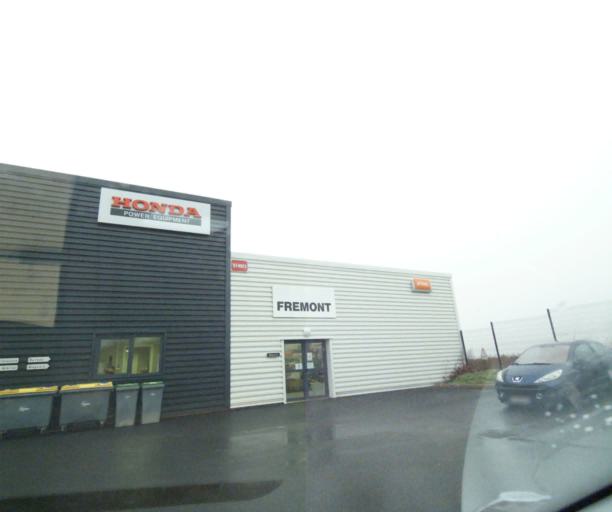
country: FR
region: Ile-de-France
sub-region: Departement de Seine-et-Marne
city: Othis
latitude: 49.0668
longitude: 2.6834
